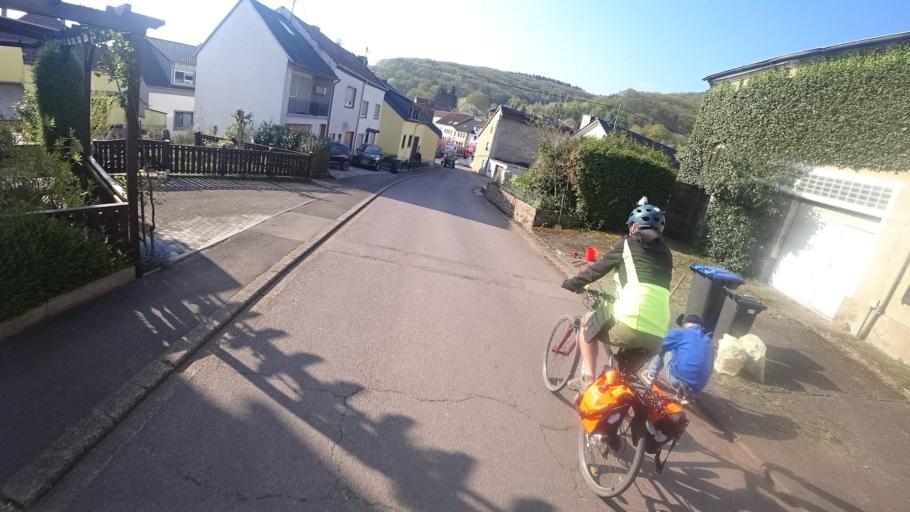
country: DE
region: Rheinland-Pfalz
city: Ayl
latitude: 49.6296
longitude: 6.5524
